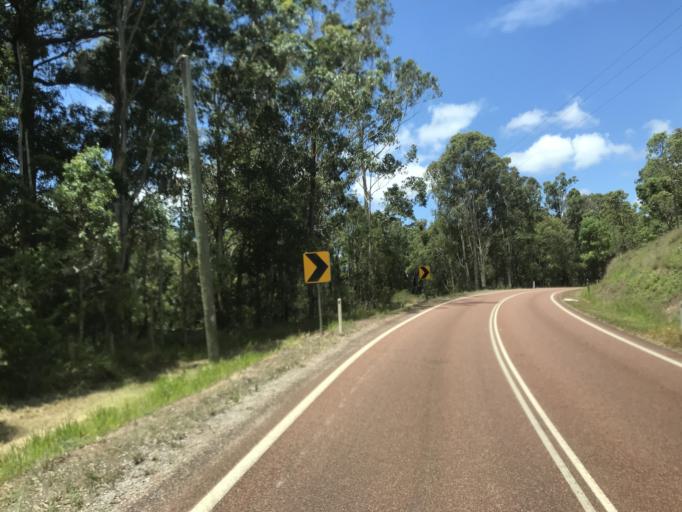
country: AU
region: Queensland
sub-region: Tablelands
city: Ravenshoe
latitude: -17.5997
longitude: 145.4773
